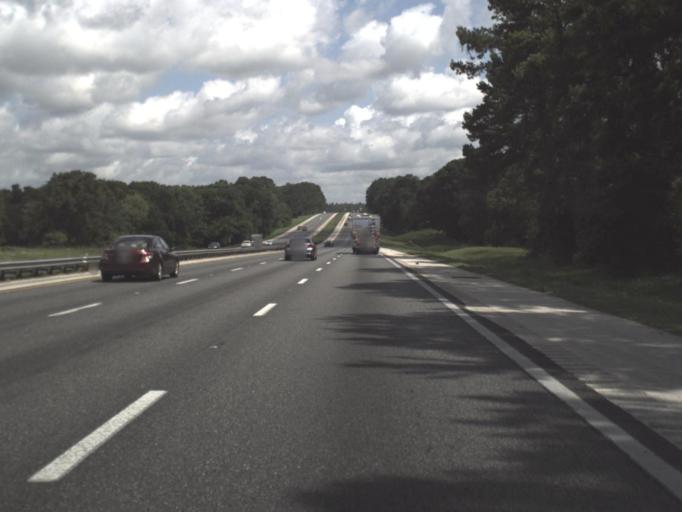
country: US
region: Florida
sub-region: Alachua County
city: High Springs
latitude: 29.8405
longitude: -82.5288
